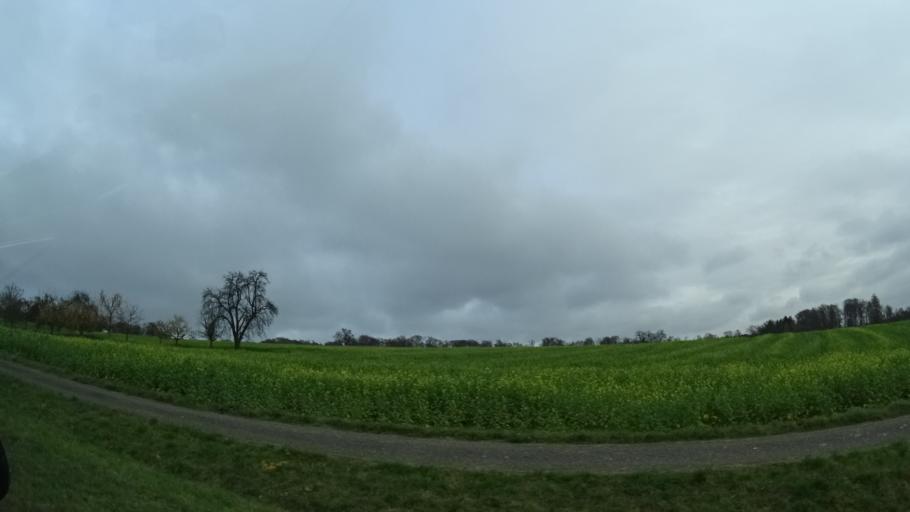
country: DE
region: Baden-Wuerttemberg
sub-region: Karlsruhe Region
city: Neckargerach
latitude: 49.4257
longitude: 9.0842
